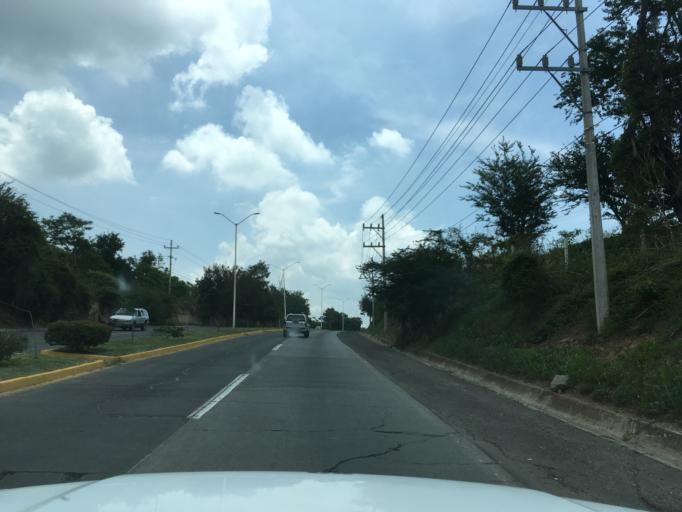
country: MX
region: Jalisco
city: Tlajomulco de Zuniga
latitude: 20.4896
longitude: -103.4650
